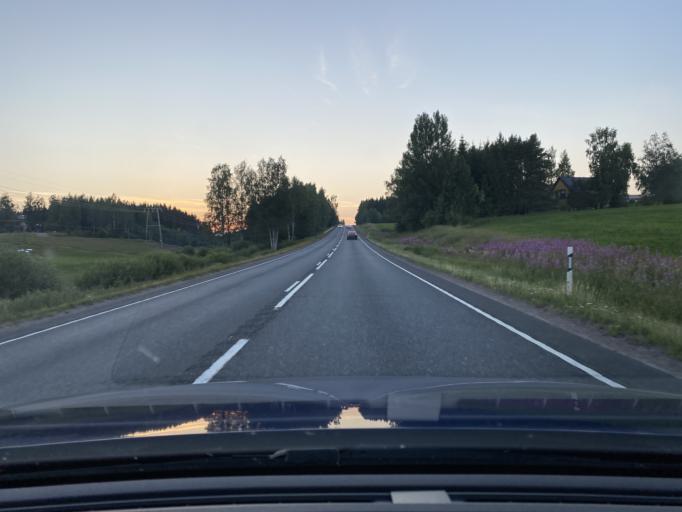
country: FI
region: Pirkanmaa
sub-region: Luoteis-Pirkanmaa
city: Ikaalinen
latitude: 61.8145
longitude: 22.9564
